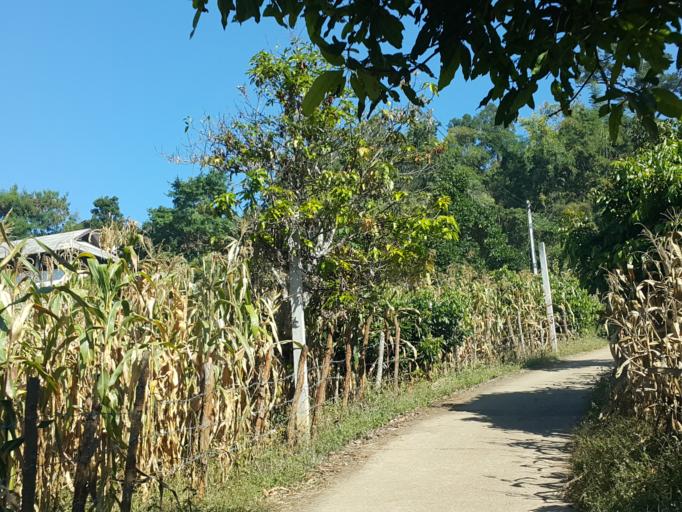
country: TH
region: Chiang Mai
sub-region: Amphoe Chiang Dao
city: Chiang Dao
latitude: 19.5228
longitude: 98.8626
